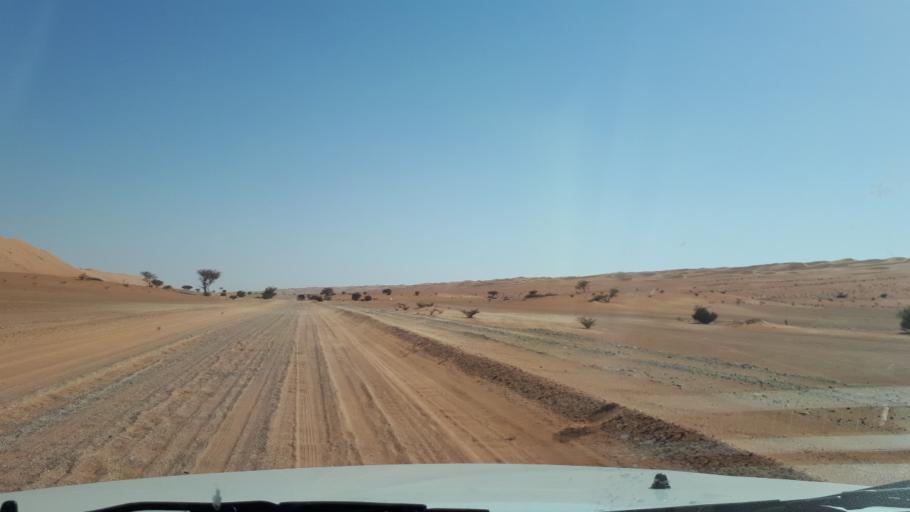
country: OM
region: Ash Sharqiyah
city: Badiyah
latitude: 22.4469
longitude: 58.7358
